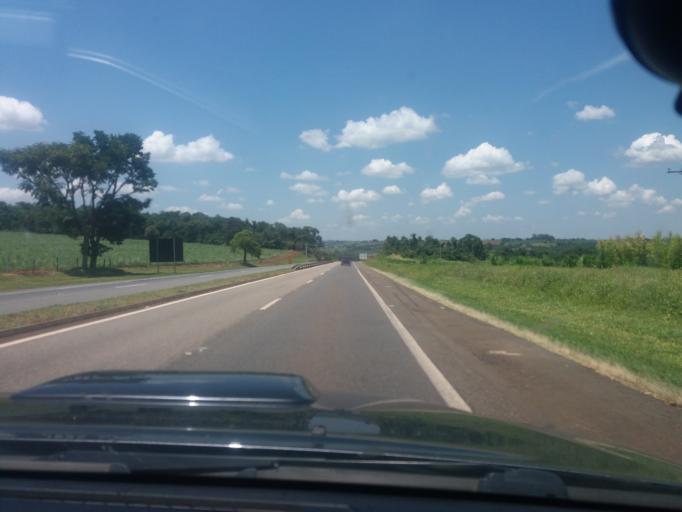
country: BR
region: Sao Paulo
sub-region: Tatui
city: Tatui
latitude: -23.4390
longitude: -47.9431
